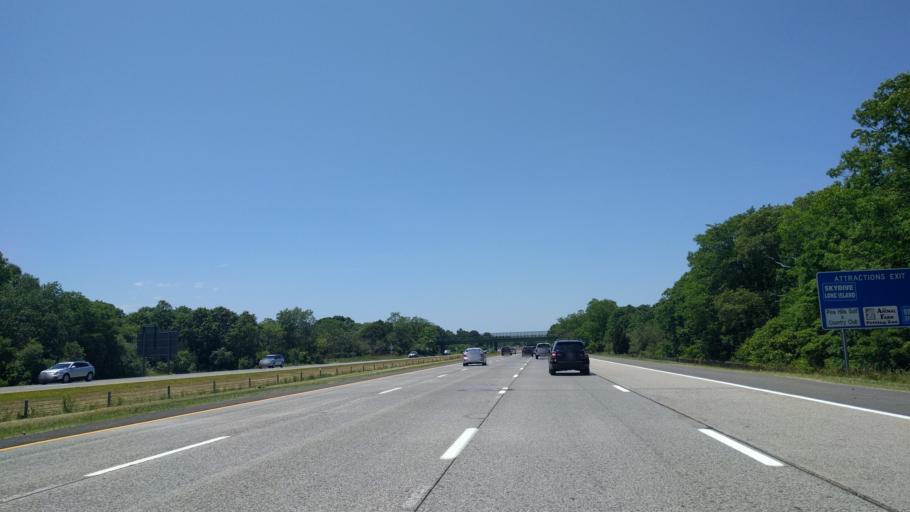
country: US
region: New York
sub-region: Suffolk County
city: Manorville
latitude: 40.8699
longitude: -72.8066
